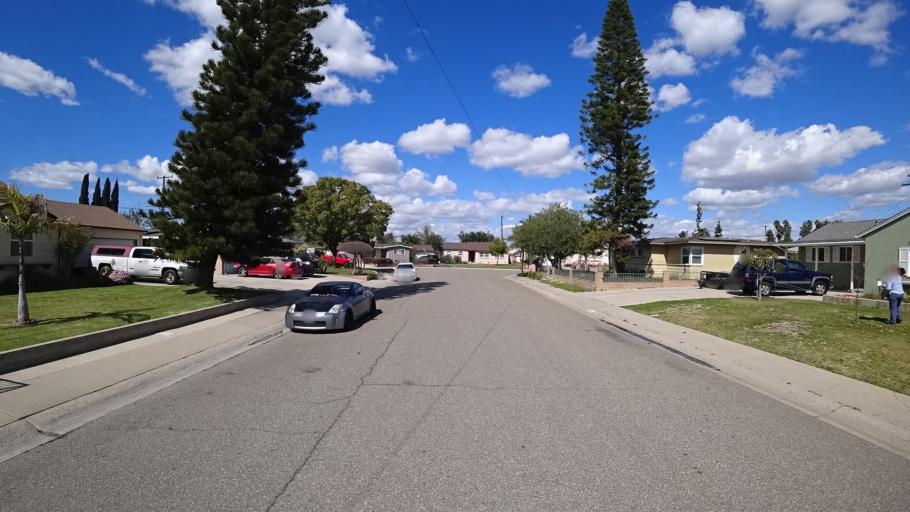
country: US
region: California
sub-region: Orange County
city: Anaheim
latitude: 33.8386
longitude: -117.8938
